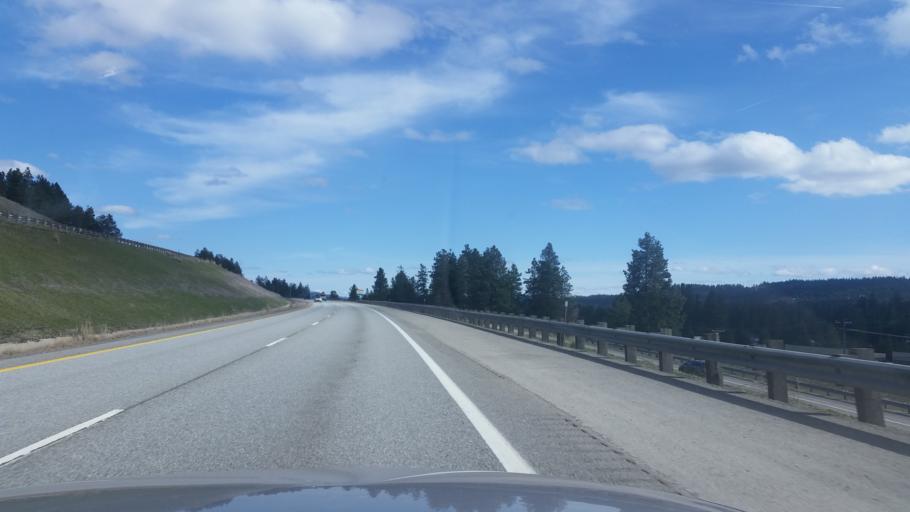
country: US
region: Idaho
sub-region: Kootenai County
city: Post Falls
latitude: 47.7097
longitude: -116.8930
